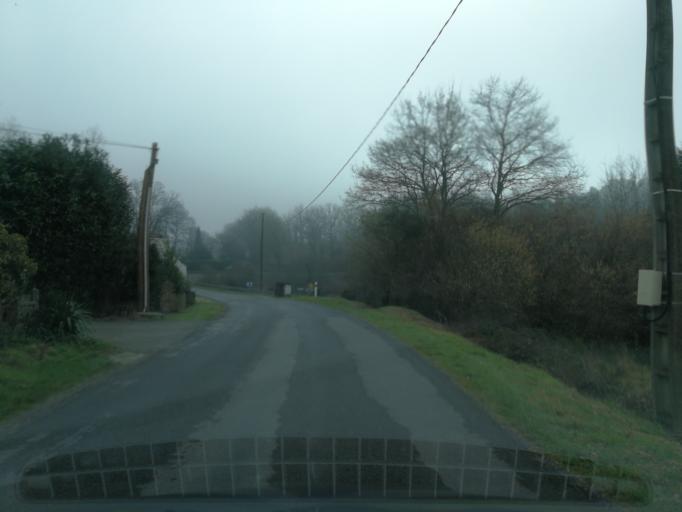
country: FR
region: Brittany
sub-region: Departement du Morbihan
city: La Vraie-Croix
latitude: 47.7327
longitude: -2.5073
